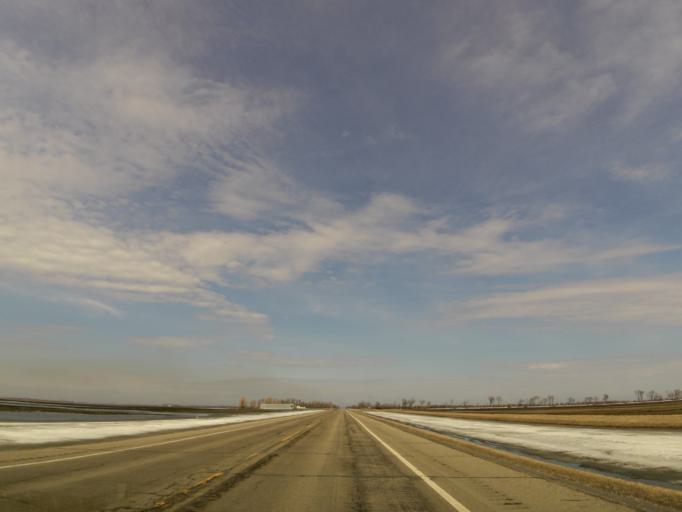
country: US
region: North Dakota
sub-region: Walsh County
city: Grafton
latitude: 48.3268
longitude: -97.4050
